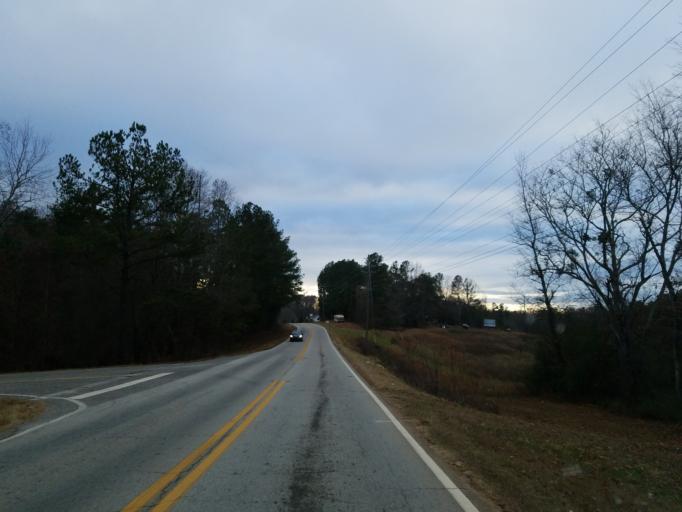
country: US
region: Georgia
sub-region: Dawson County
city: Dawsonville
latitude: 34.3771
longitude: -84.0291
